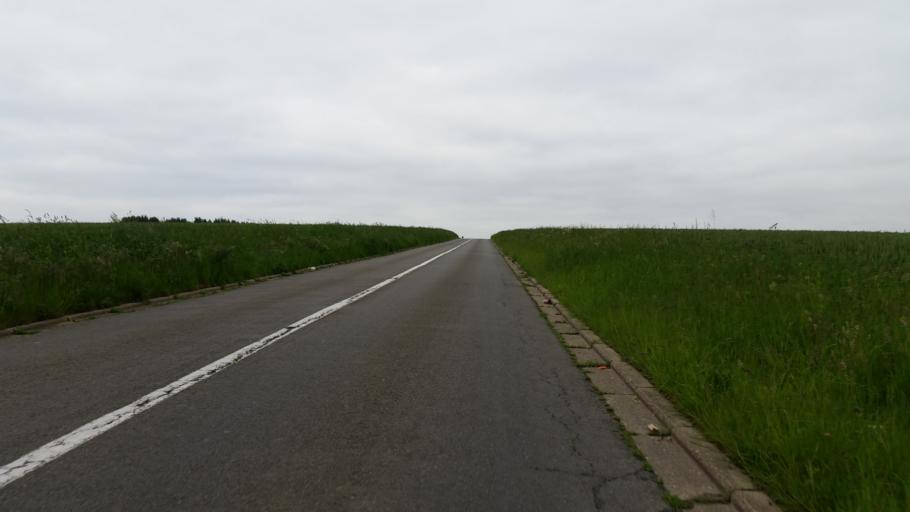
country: BE
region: Flanders
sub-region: Provincie Vlaams-Brabant
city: Grimbergen
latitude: 50.9215
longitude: 4.3808
